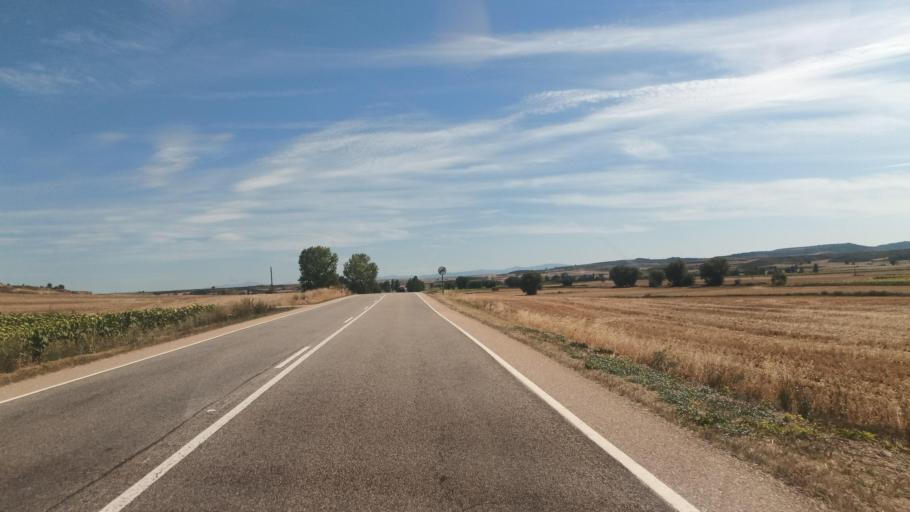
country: ES
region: Castille and Leon
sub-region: Provincia de Burgos
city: Quintanabureba
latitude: 42.6078
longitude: -3.3532
